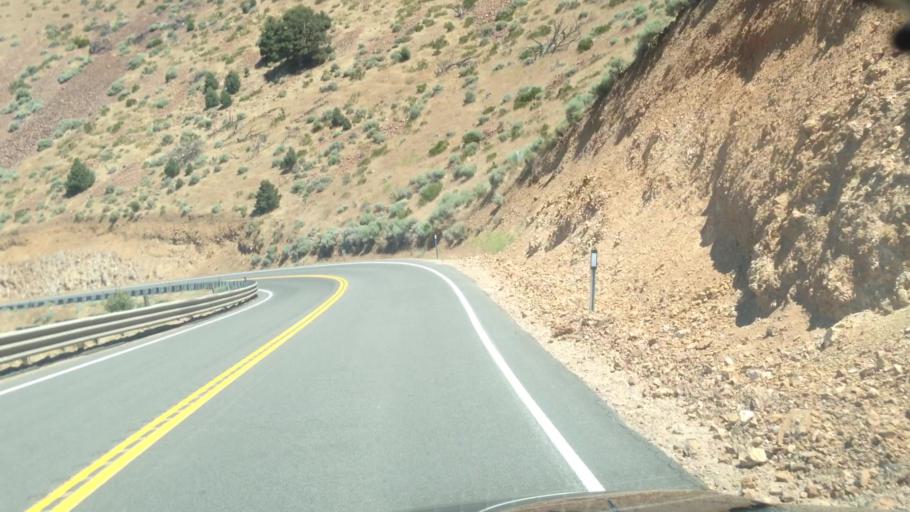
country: US
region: Nevada
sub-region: Storey County
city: Virginia City
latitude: 39.3821
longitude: -119.6967
